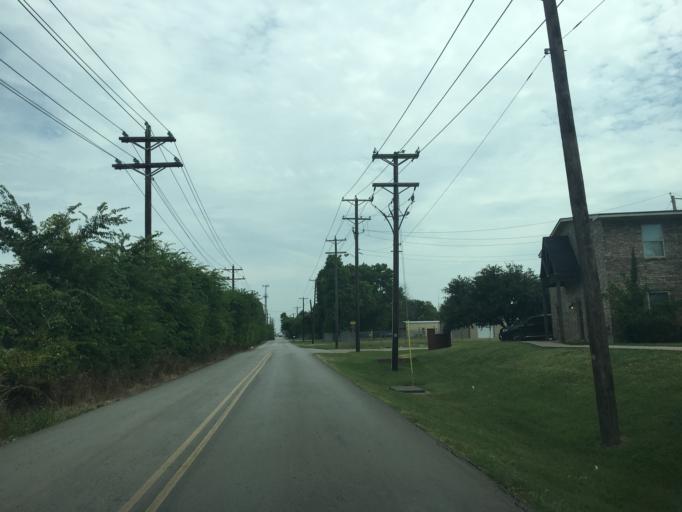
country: US
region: Texas
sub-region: Collin County
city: Wylie
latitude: 33.0182
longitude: -96.5196
